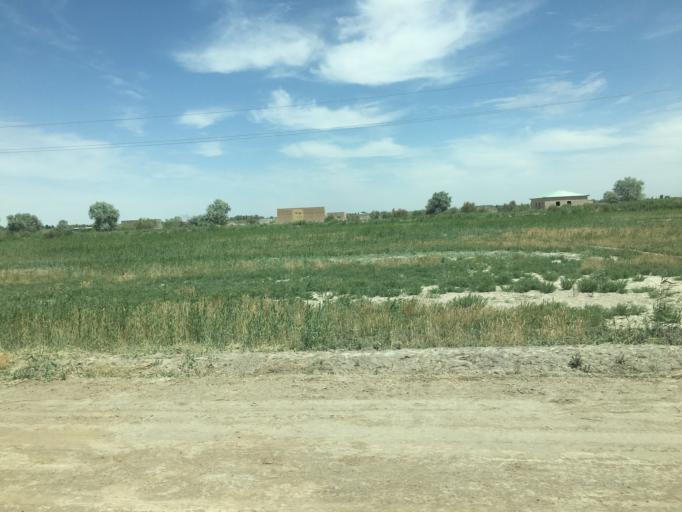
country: TM
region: Dasoguz
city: Tagta
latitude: 41.7080
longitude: 59.9371
